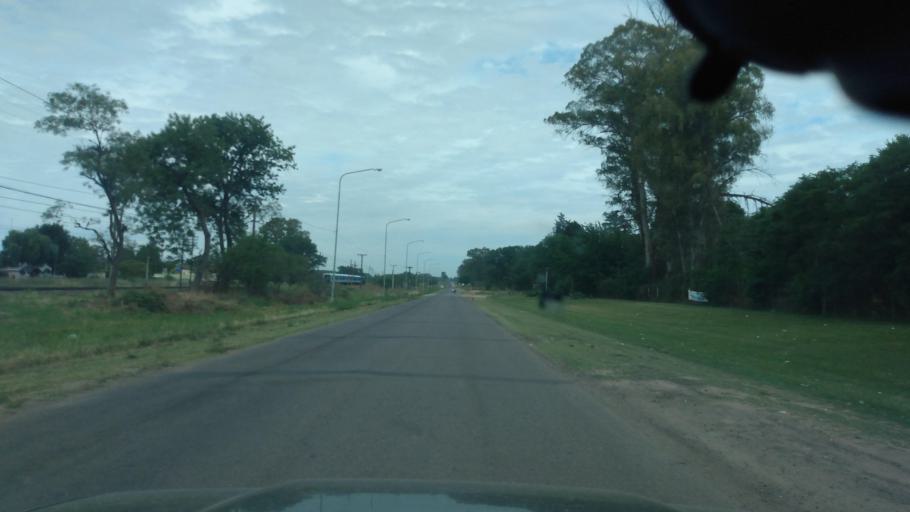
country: AR
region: Buenos Aires
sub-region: Partido de Lujan
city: Lujan
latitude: -34.5838
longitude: -59.0584
